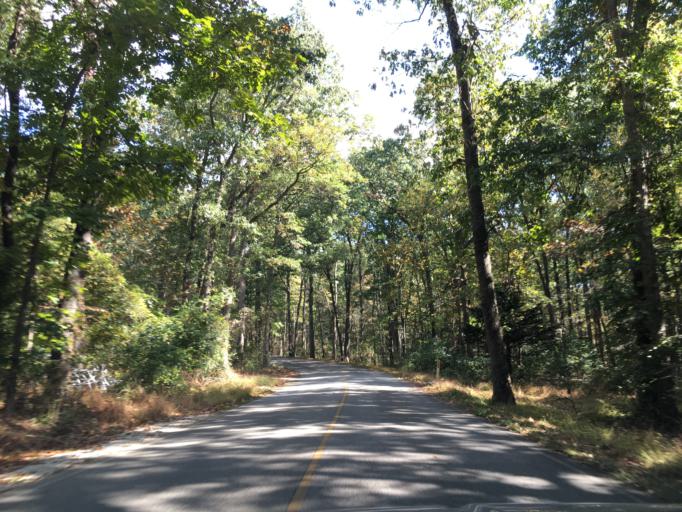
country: US
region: Pennsylvania
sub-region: York County
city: Yorklyn
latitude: 40.0111
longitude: -76.6553
